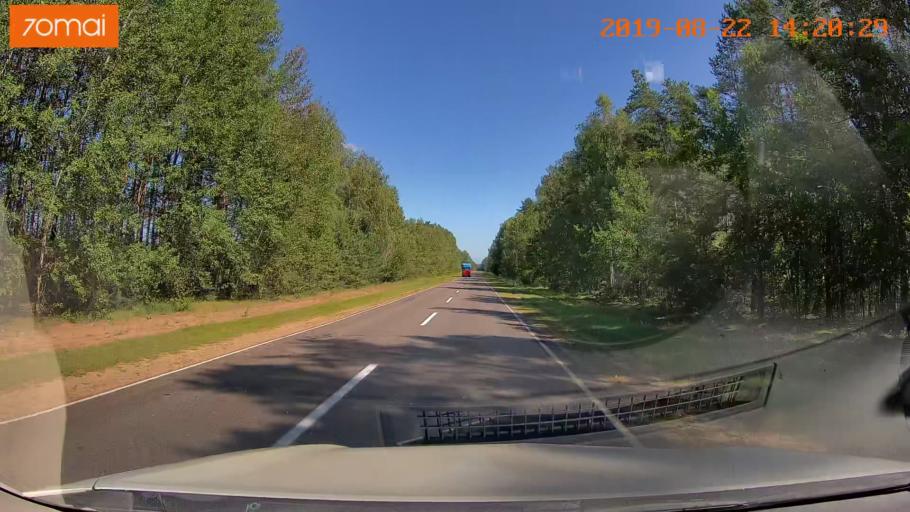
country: BY
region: Mogilev
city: Asipovichy
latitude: 53.2647
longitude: 28.5276
